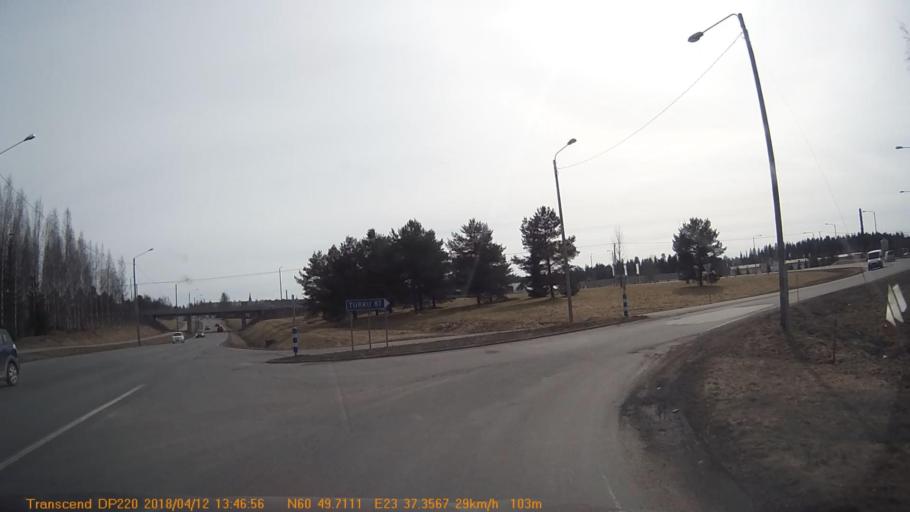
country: FI
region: Haeme
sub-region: Forssa
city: Forssa
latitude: 60.8284
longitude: 23.6226
